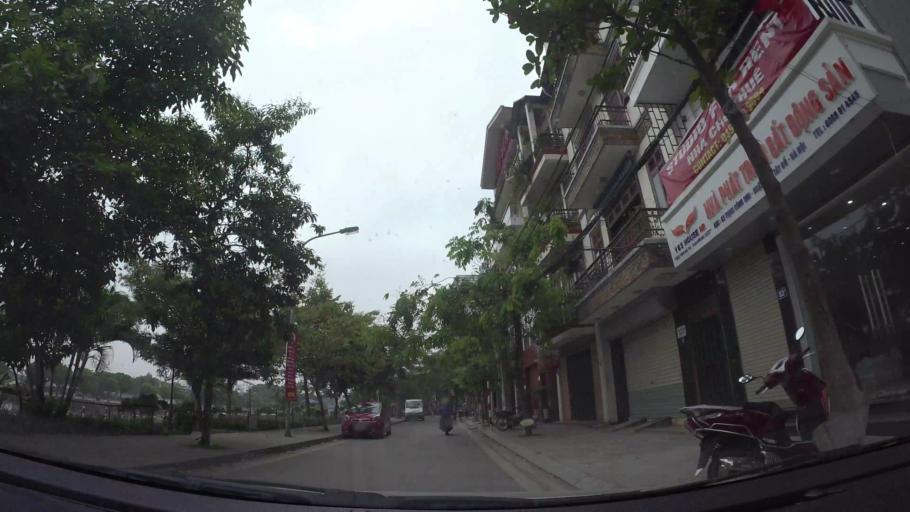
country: VN
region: Ha Noi
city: Tay Ho
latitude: 21.0779
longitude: 105.8176
